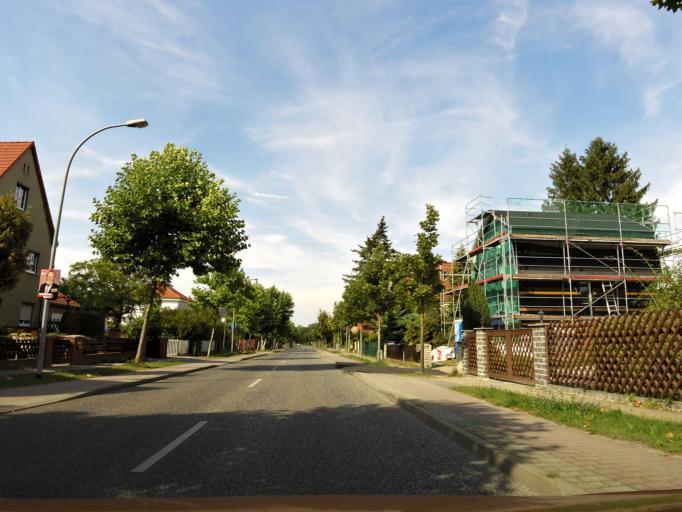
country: DE
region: Brandenburg
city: Teltow
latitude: 52.3883
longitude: 13.2465
